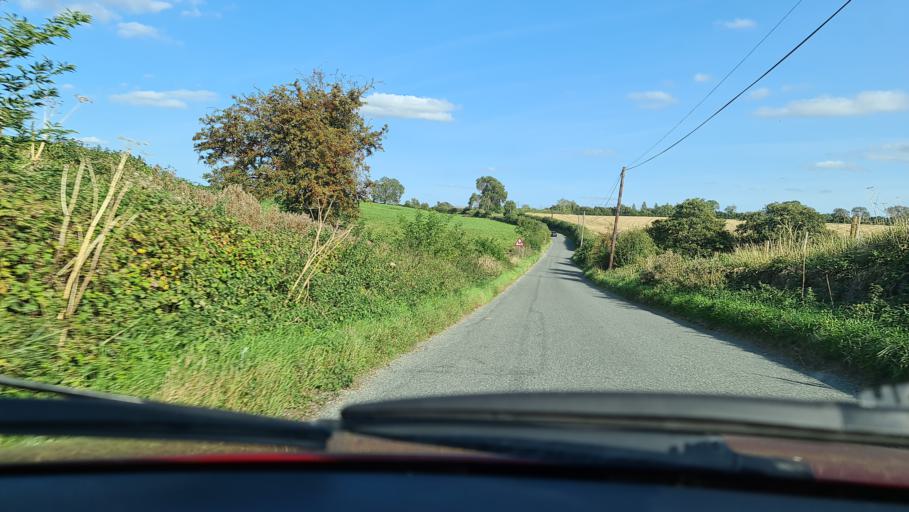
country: GB
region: England
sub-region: Northamptonshire
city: Brackley
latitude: 52.0214
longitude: -1.2265
